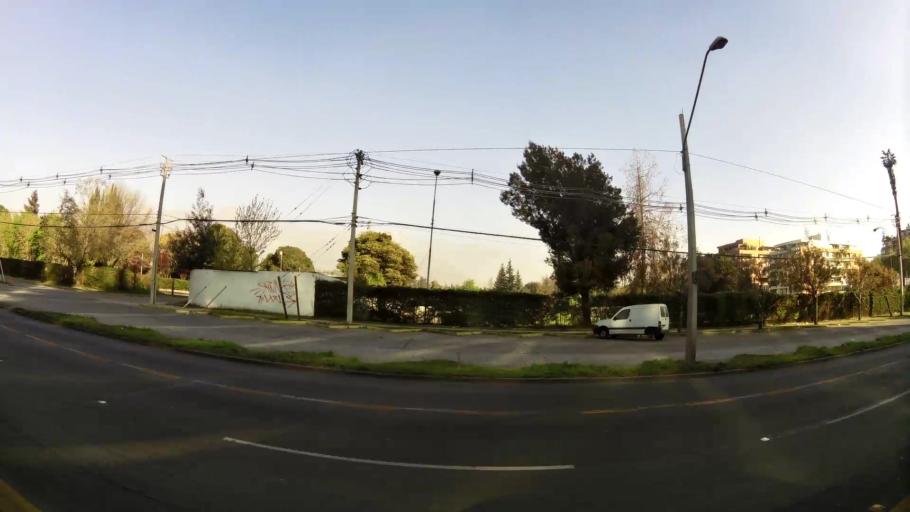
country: CL
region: Santiago Metropolitan
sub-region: Provincia de Santiago
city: Villa Presidente Frei, Nunoa, Santiago, Chile
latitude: -33.3756
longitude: -70.5243
